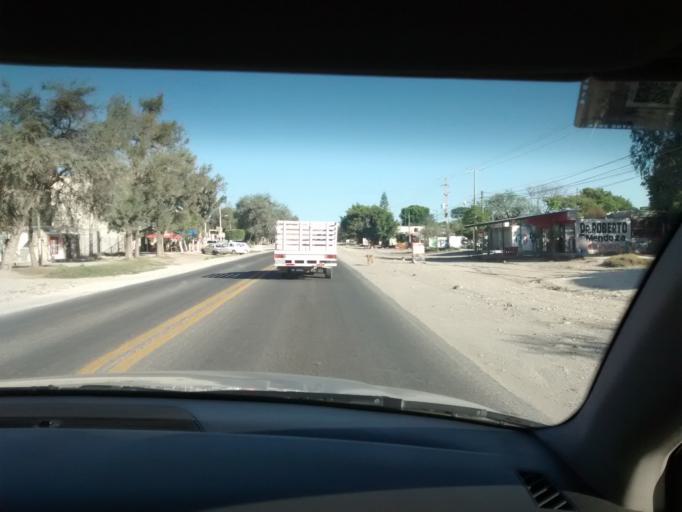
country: MX
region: Puebla
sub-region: Tehuacan
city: Magdalena Cuayucatepec
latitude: 18.5095
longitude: -97.4901
